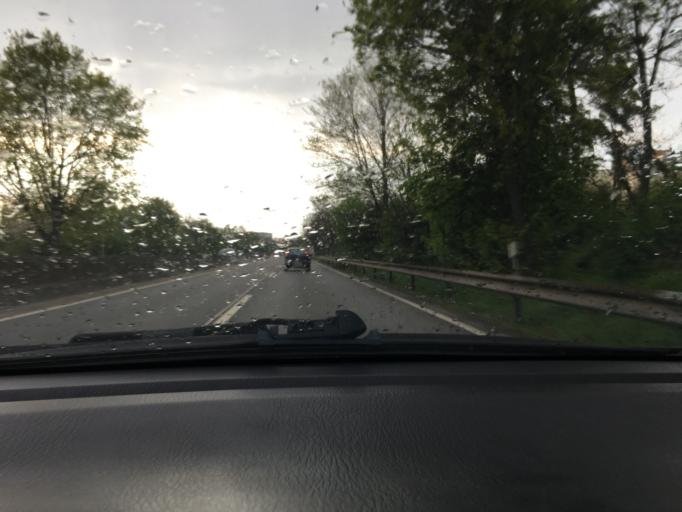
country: DE
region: Rheinland-Pfalz
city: Sankt Sebastian
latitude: 50.4173
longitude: 7.5729
